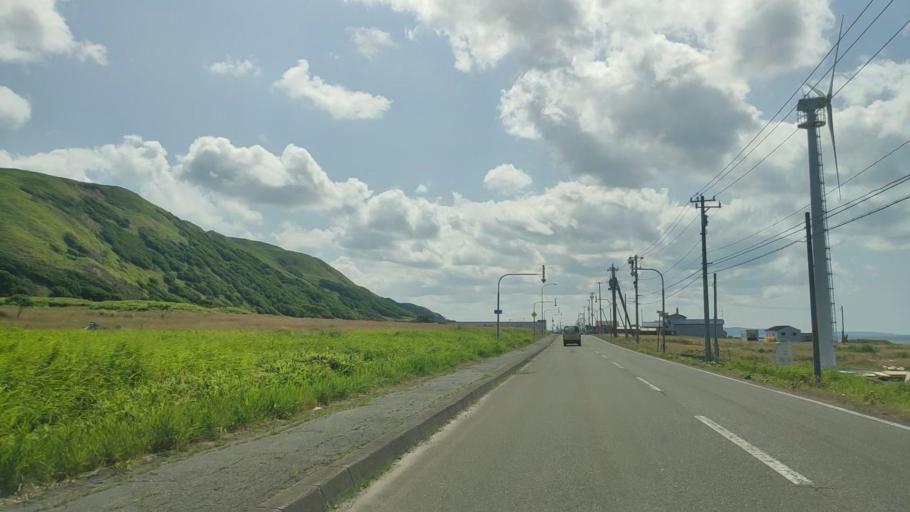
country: JP
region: Hokkaido
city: Wakkanai
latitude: 45.4004
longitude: 141.6372
